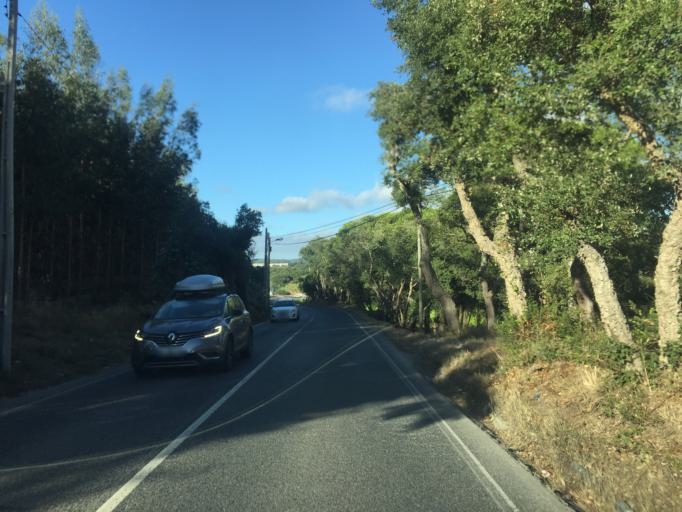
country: PT
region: Lisbon
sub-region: Torres Vedras
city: A dos Cunhados
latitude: 39.1474
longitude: -9.2748
